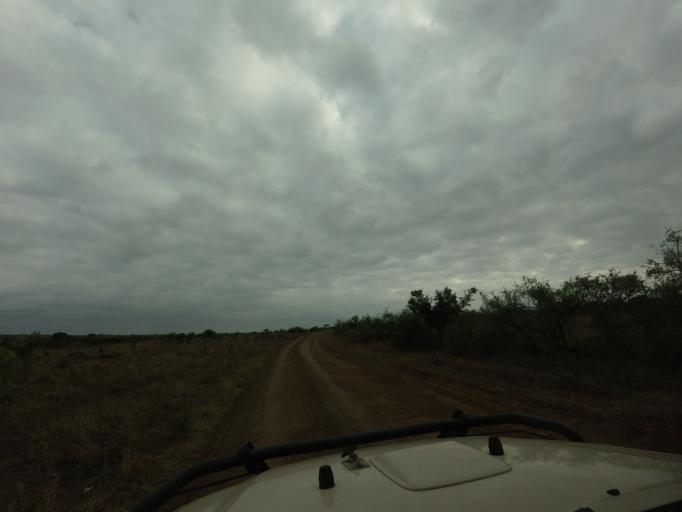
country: ZA
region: Mpumalanga
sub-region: Ehlanzeni District
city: Komatipoort
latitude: -25.3208
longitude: 31.9072
